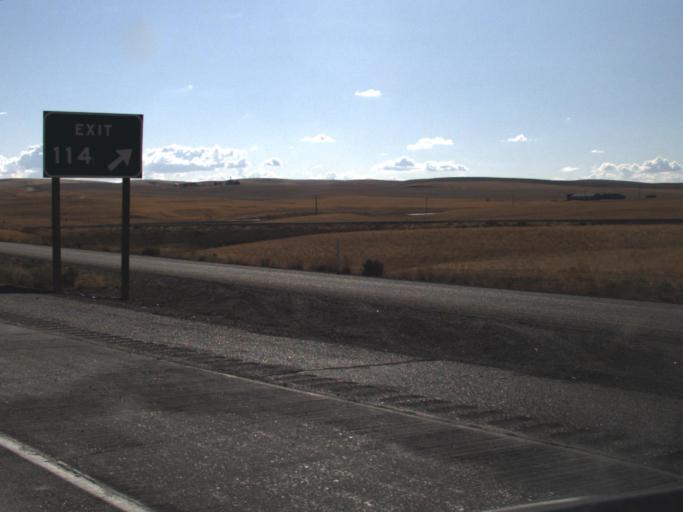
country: US
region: Washington
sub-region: Benton County
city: Highland
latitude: 46.1453
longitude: -119.2022
